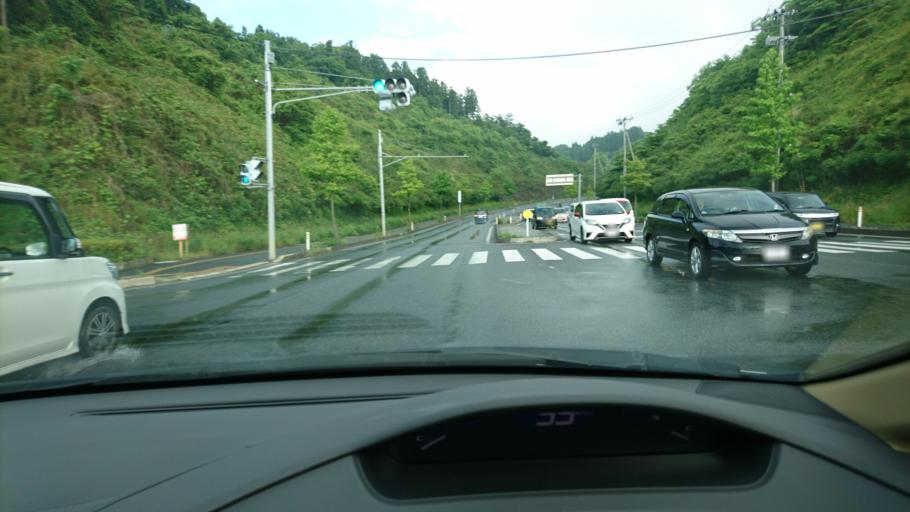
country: JP
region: Iwate
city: Ichinoseki
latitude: 38.9339
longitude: 141.1644
